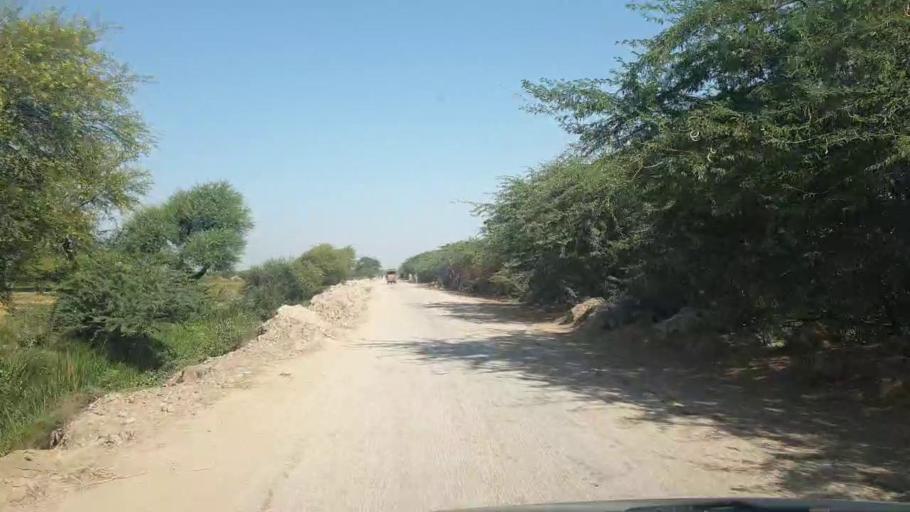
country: PK
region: Sindh
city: Tando Bago
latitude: 24.8023
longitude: 68.9780
